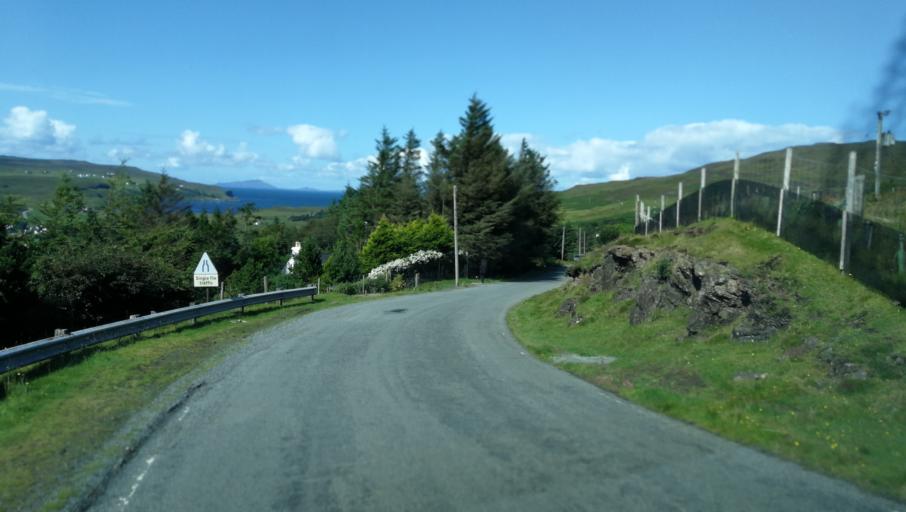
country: GB
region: Scotland
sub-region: Highland
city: Isle of Skye
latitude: 57.4482
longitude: -6.6903
